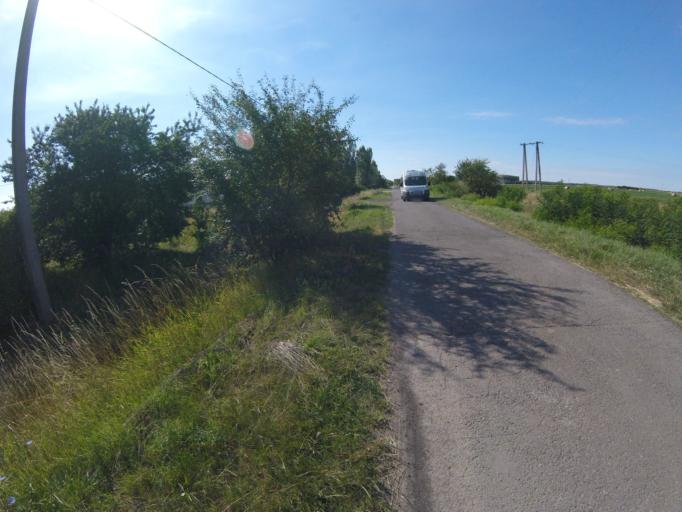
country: HU
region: Heves
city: Tiszanana
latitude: 47.5806
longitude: 20.6032
